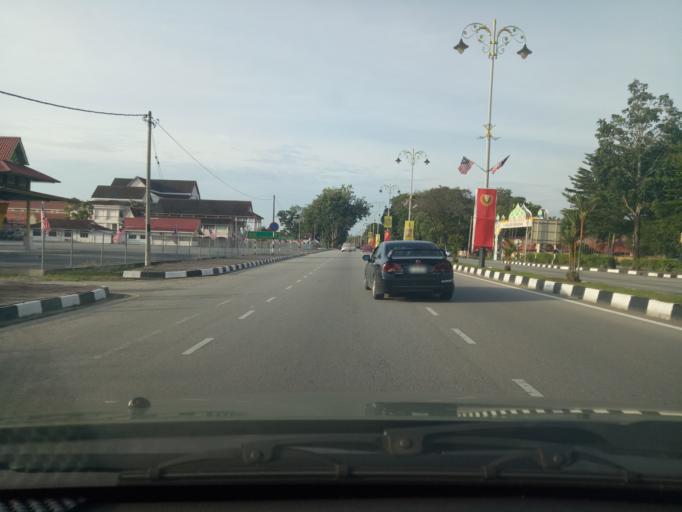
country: MY
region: Kedah
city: Alor Setar
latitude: 6.1344
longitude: 100.3691
